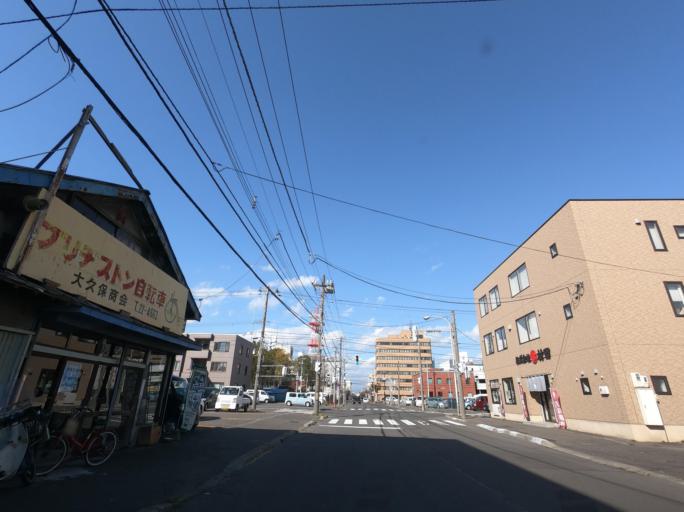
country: JP
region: Hokkaido
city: Kushiro
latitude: 42.9833
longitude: 144.3830
